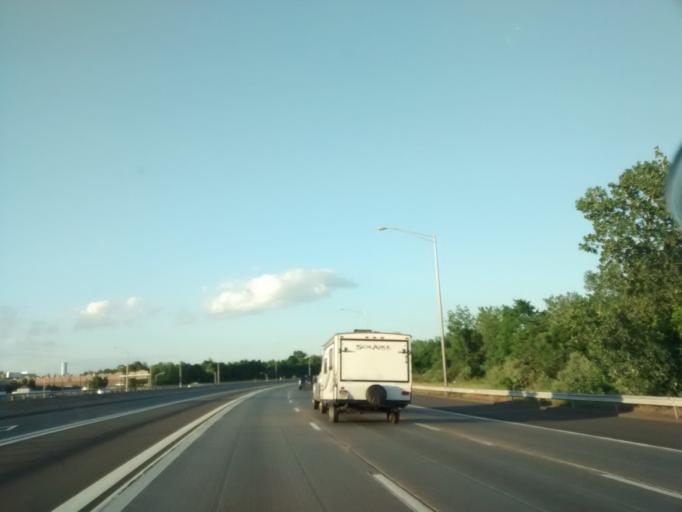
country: US
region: Connecticut
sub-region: Hartford County
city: Manchester
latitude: 41.8003
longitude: -72.5546
